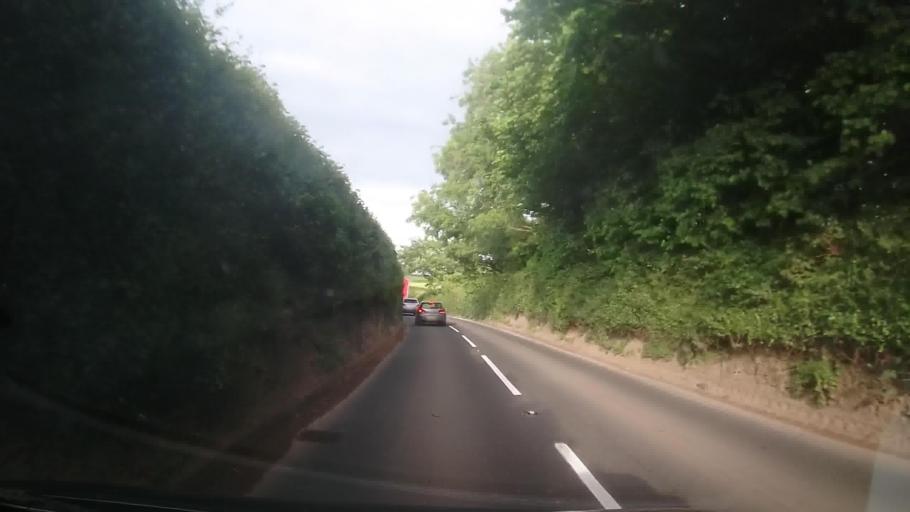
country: GB
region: England
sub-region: Devon
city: Kingsbridge
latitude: 50.2978
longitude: -3.8024
